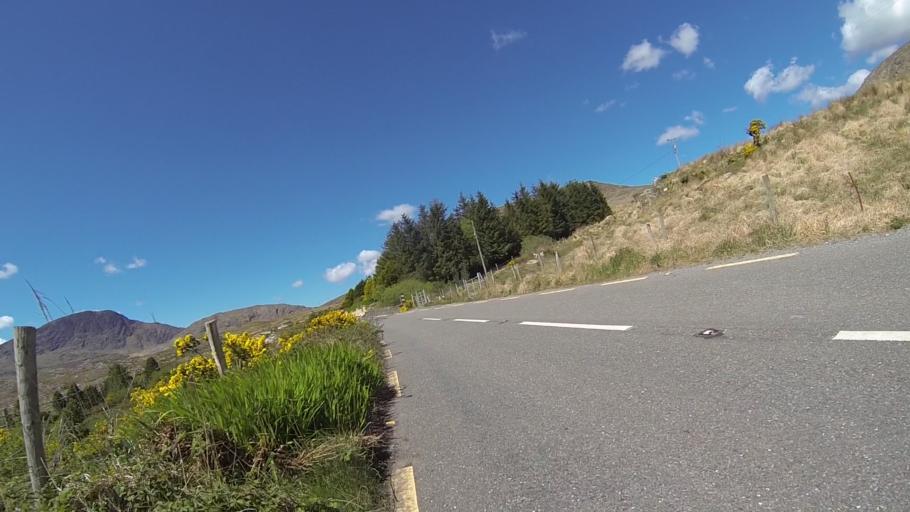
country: IE
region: Munster
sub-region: Ciarrai
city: Kenmare
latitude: 51.9247
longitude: -9.6324
